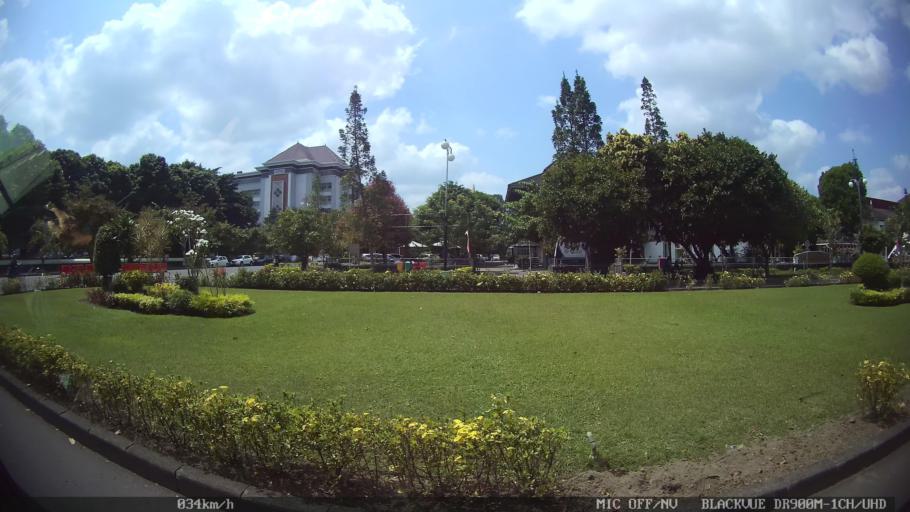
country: ID
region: Daerah Istimewa Yogyakarta
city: Yogyakarta
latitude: -7.7725
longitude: 110.3770
